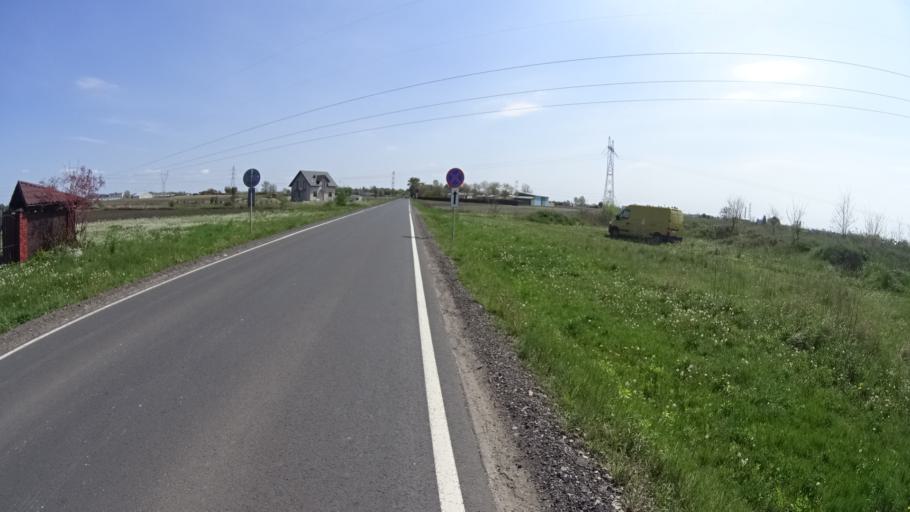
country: PL
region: Masovian Voivodeship
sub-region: Powiat warszawski zachodni
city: Ozarow Mazowiecki
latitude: 52.2384
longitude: 20.7539
